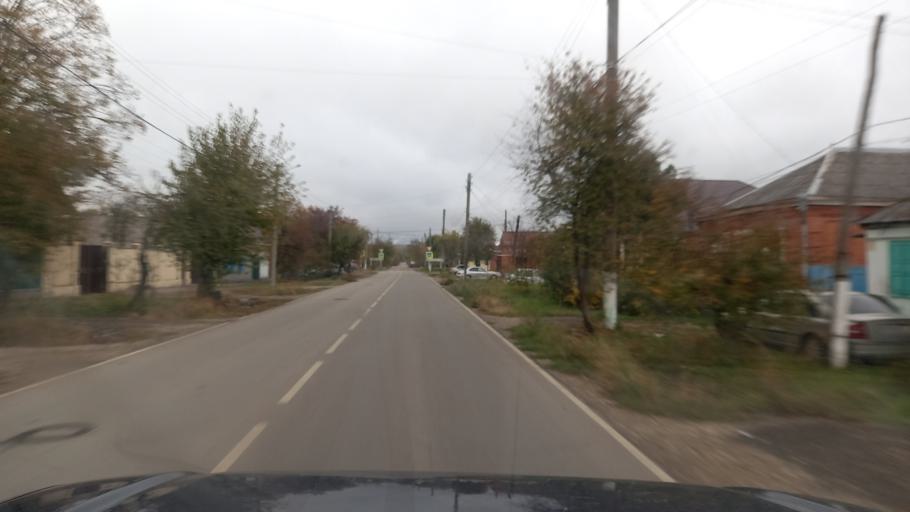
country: RU
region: Adygeya
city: Maykop
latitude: 44.6105
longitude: 40.1254
